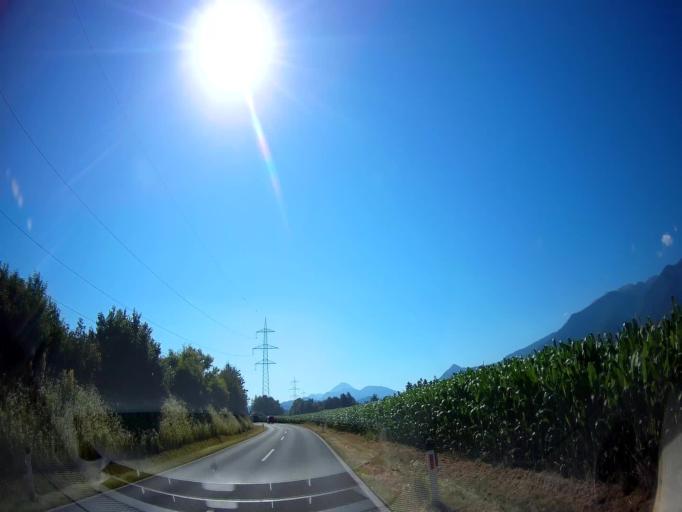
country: AT
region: Carinthia
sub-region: Politischer Bezirk Volkermarkt
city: Feistritz ob Bleiburg
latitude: 46.5742
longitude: 14.7452
